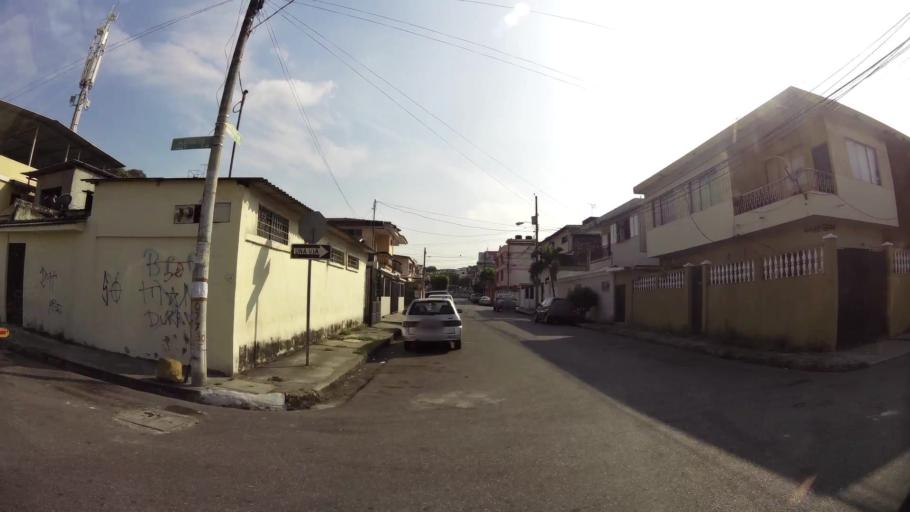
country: EC
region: Guayas
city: Guayaquil
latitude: -2.1877
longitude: -79.9042
